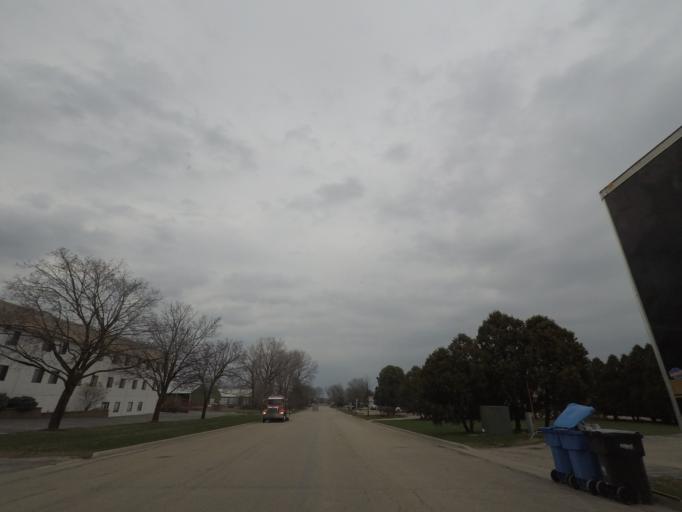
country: US
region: Wisconsin
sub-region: Dane County
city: Middleton
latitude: 43.1000
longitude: -89.5322
